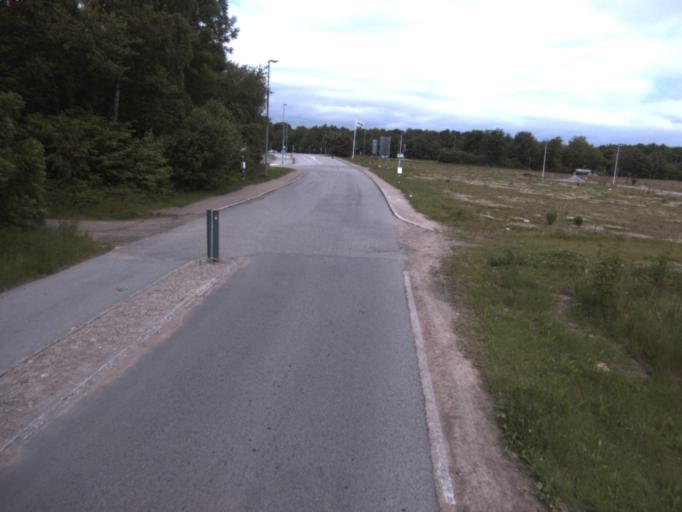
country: SE
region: Skane
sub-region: Helsingborg
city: Odakra
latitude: 56.0601
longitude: 12.7360
